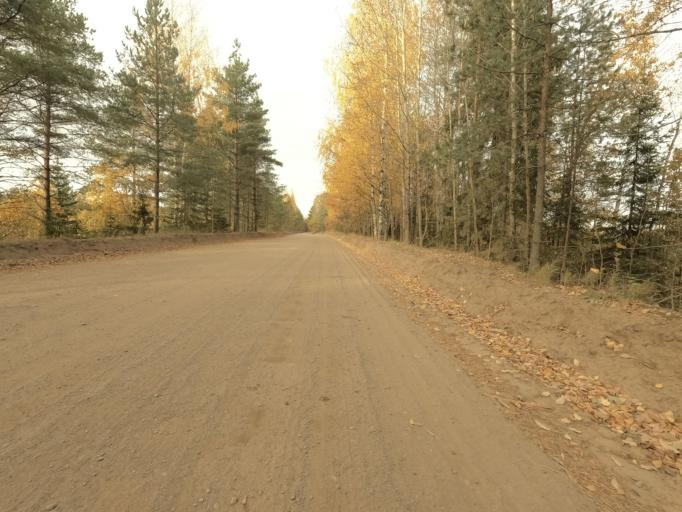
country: RU
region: Leningrad
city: Priladozhskiy
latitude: 59.6763
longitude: 31.3658
